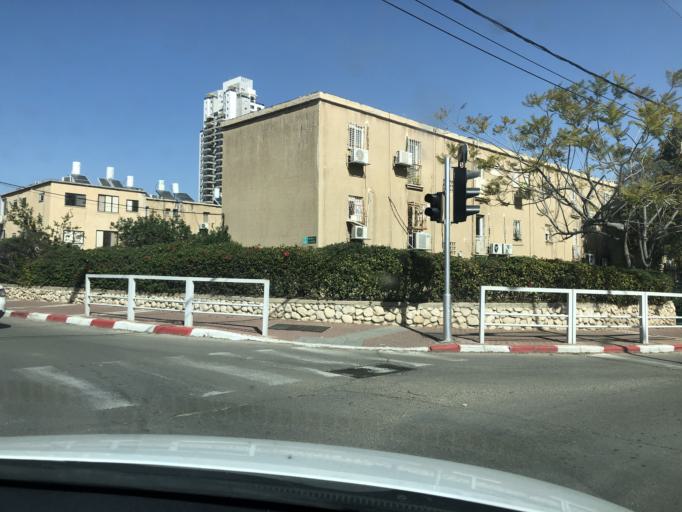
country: IL
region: Southern District
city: Beersheba
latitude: 31.2556
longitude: 34.7951
